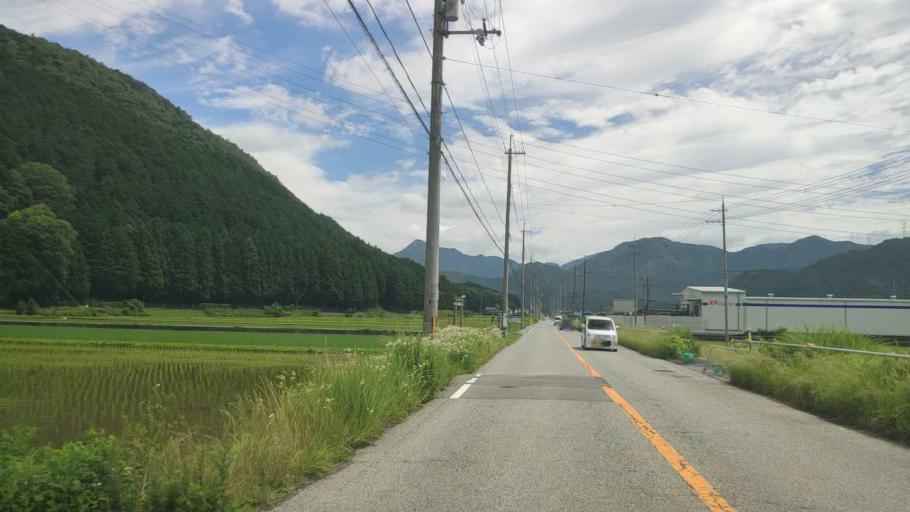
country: JP
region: Hyogo
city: Nishiwaki
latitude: 35.1108
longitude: 134.9102
